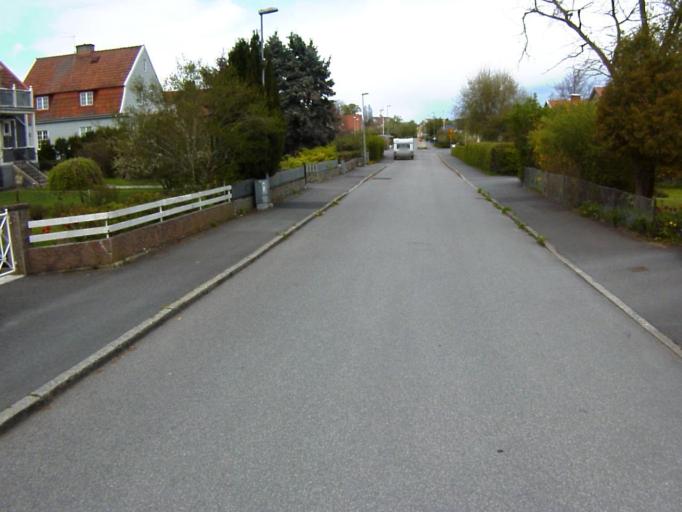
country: SE
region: Skane
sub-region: Kristianstads Kommun
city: Kristianstad
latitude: 56.0390
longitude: 14.1698
